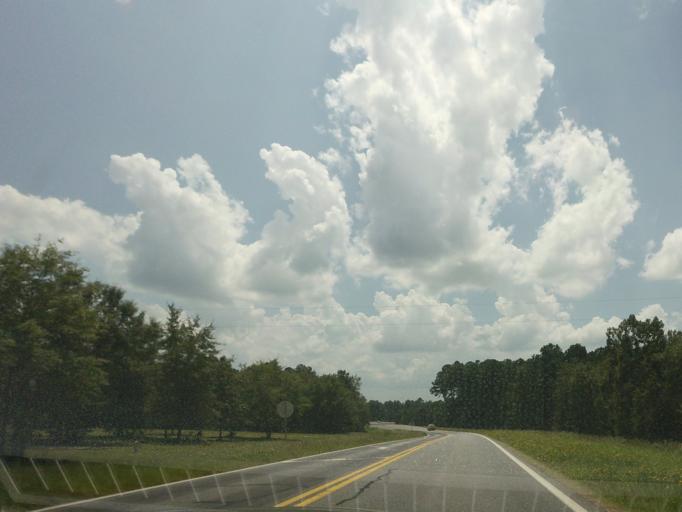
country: US
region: Georgia
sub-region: Bleckley County
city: Cochran
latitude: 32.3771
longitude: -83.3315
